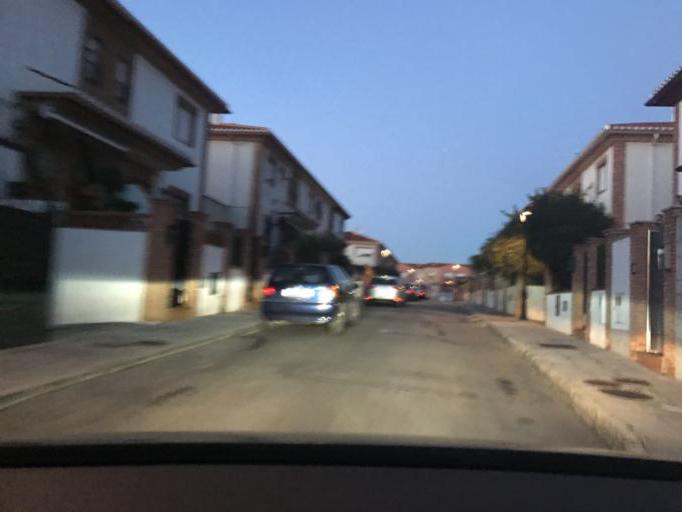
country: ES
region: Andalusia
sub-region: Provincia de Granada
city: Gojar
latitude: 37.1070
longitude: -3.6056
